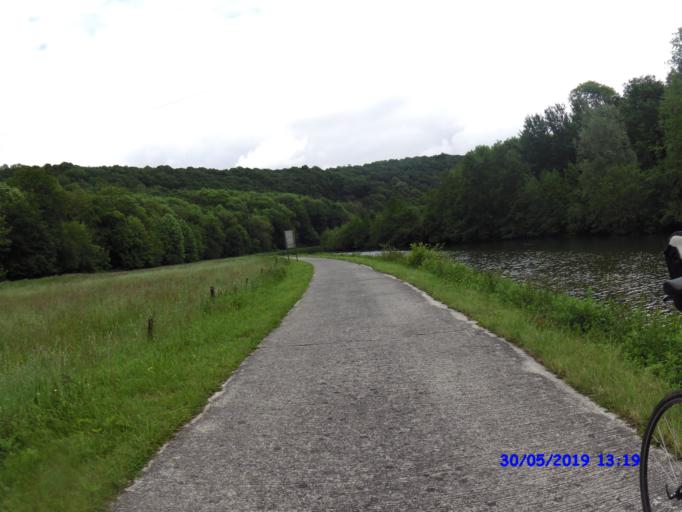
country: BE
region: Wallonia
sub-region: Province du Hainaut
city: Thuin
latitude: 50.3730
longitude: 4.3221
